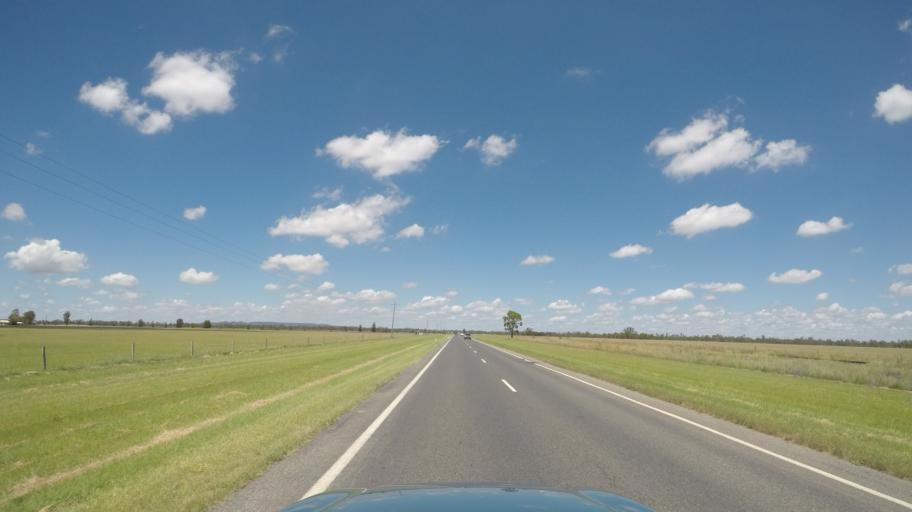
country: AU
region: Queensland
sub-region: Toowoomba
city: Oakey
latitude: -27.8629
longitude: 151.2995
